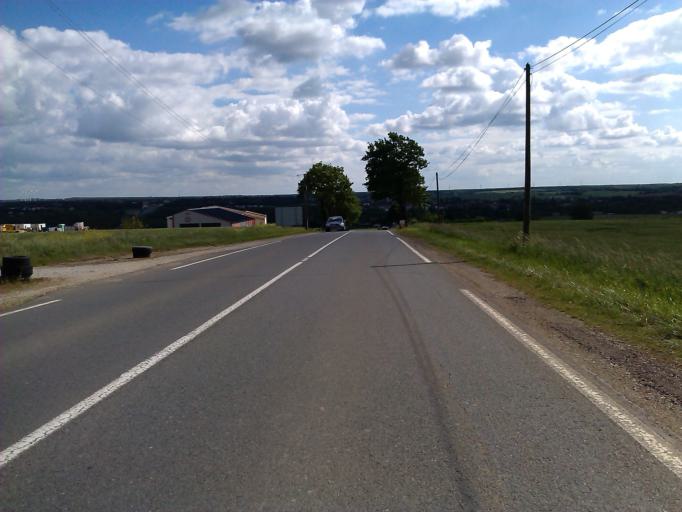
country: FR
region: Poitou-Charentes
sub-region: Departement de la Charente
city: Mansle
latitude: 45.8906
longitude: 0.1891
